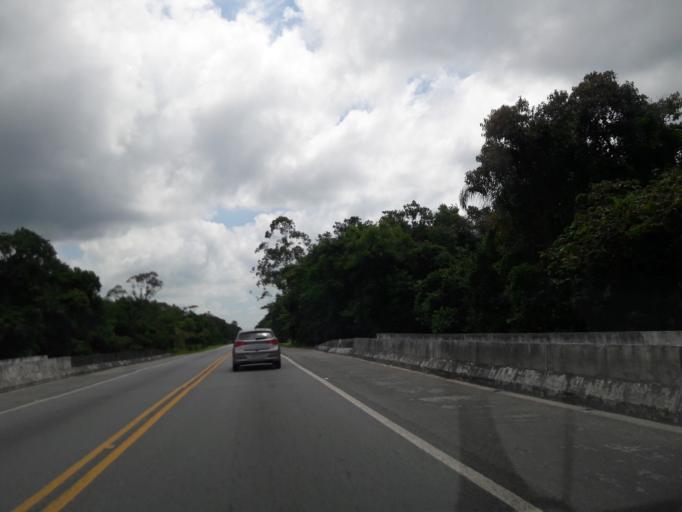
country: BR
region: Parana
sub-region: Pontal Do Parana
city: Pontal do Parana
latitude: -25.6649
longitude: -48.5185
